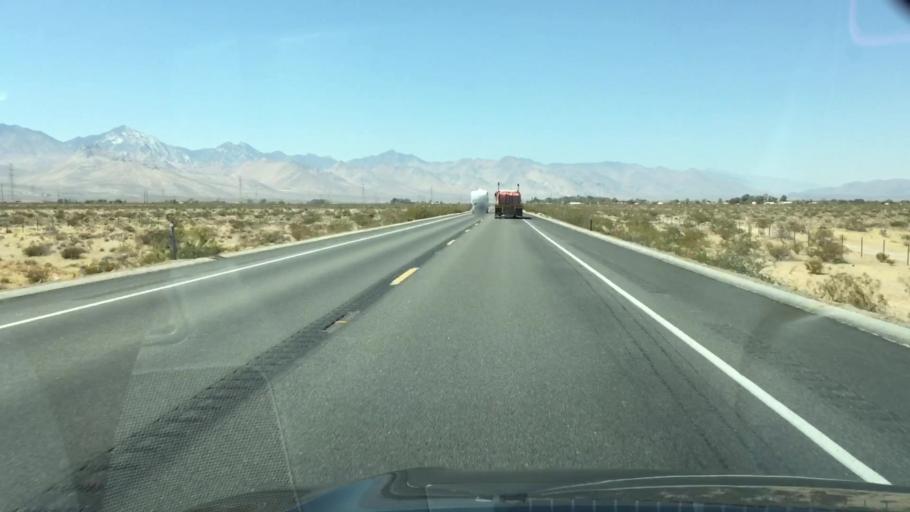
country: US
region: California
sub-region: Kern County
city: China Lake Acres
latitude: 35.6239
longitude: -117.7767
